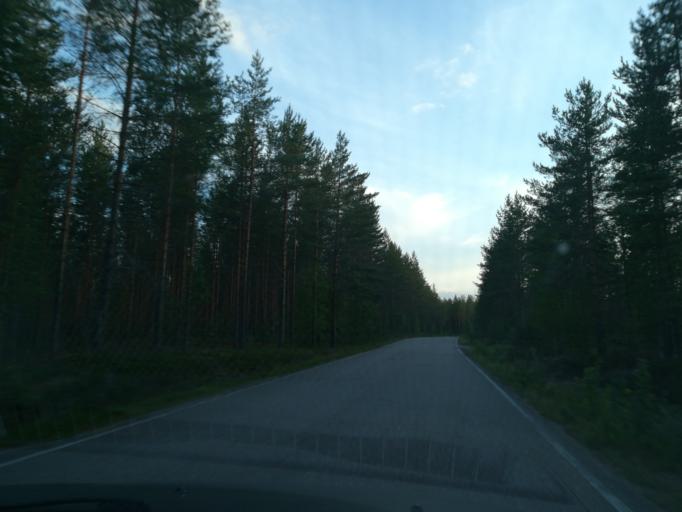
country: FI
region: South Karelia
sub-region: Lappeenranta
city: Joutseno
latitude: 61.3447
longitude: 28.4114
